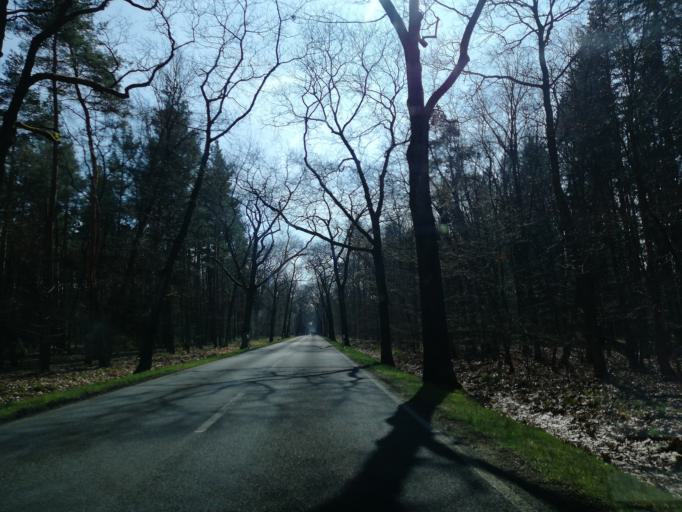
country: DE
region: Brandenburg
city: Altdobern
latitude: 51.6583
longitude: 14.0390
